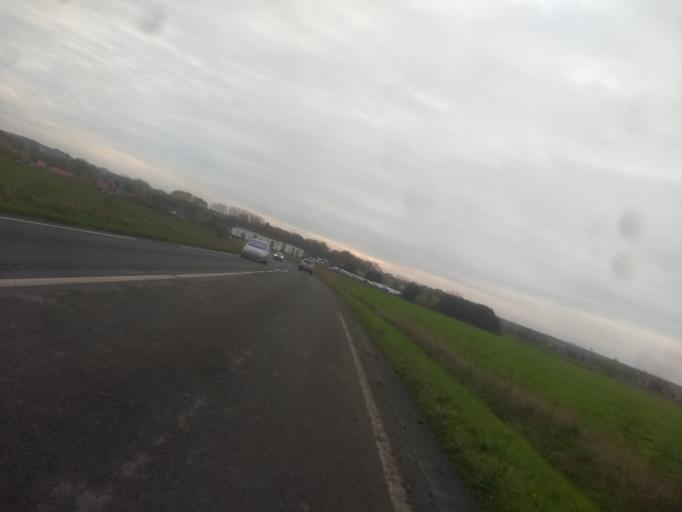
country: FR
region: Nord-Pas-de-Calais
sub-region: Departement du Pas-de-Calais
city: Achicourt
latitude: 50.2702
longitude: 2.7468
